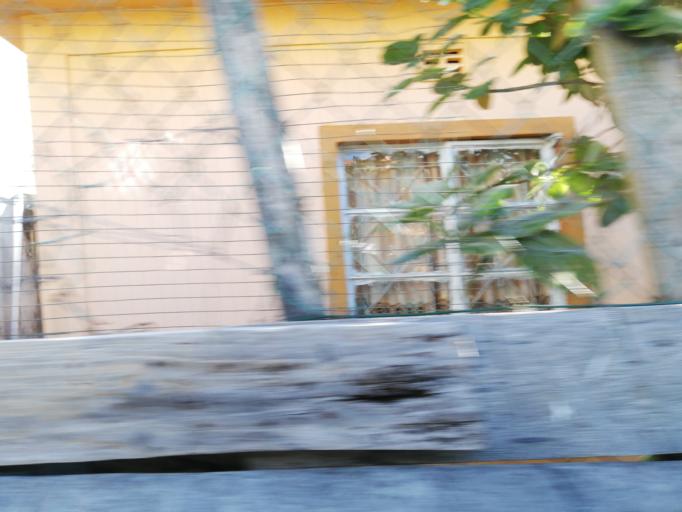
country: MU
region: Moka
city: Saint Pierre
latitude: -20.2214
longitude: 57.5298
